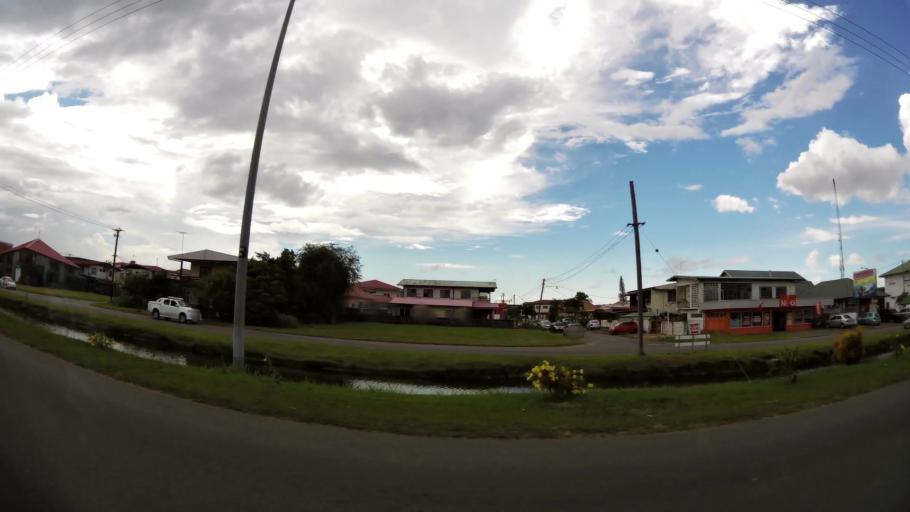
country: SR
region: Paramaribo
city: Paramaribo
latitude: 5.8479
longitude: -55.1354
